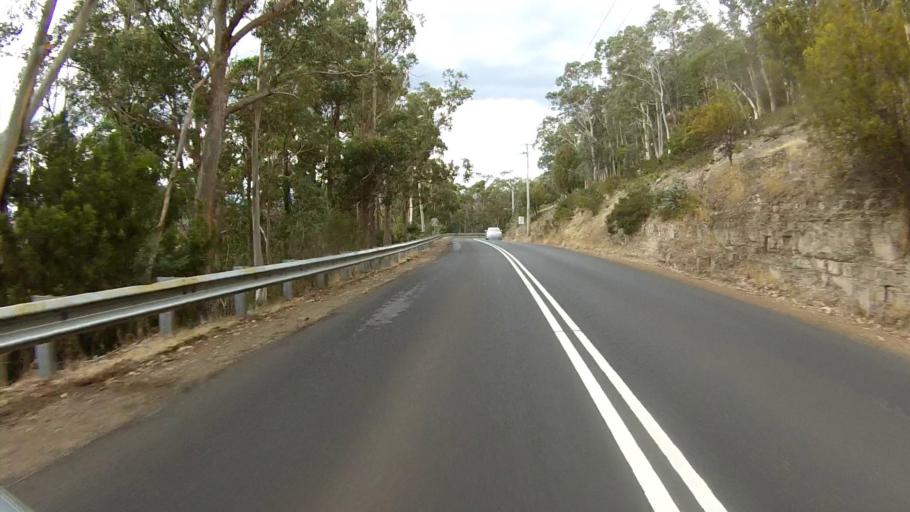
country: AU
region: Tasmania
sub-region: Hobart
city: Dynnyrne
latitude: -42.9056
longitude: 147.2771
